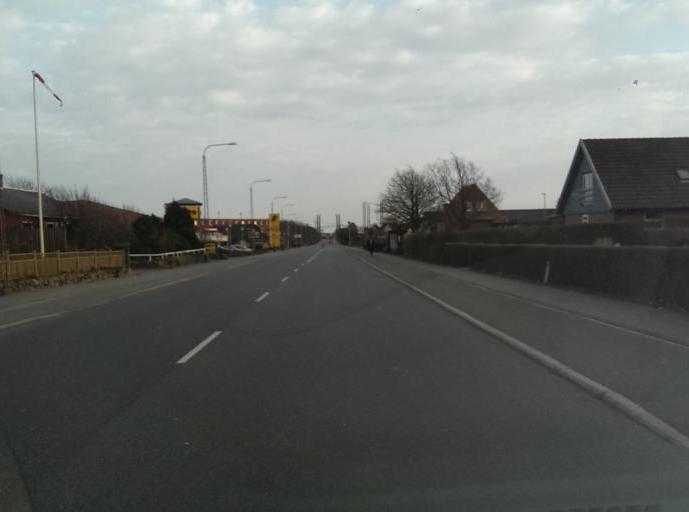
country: DK
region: South Denmark
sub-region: Esbjerg Kommune
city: Esbjerg
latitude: 55.4954
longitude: 8.4092
